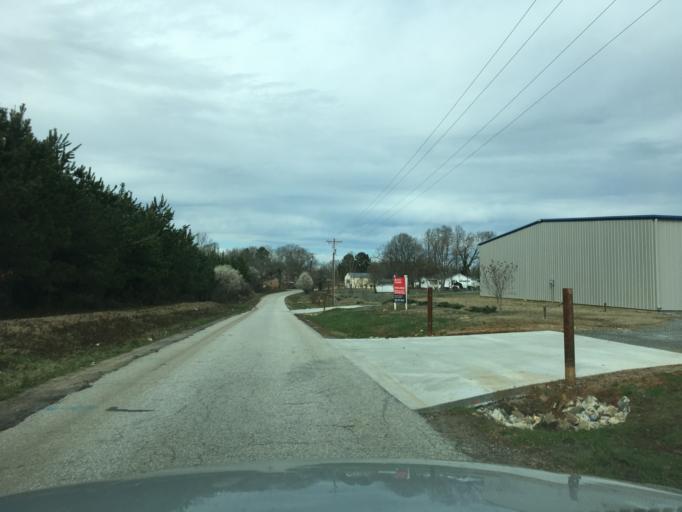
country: US
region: South Carolina
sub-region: Spartanburg County
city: Duncan
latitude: 34.9160
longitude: -82.1848
